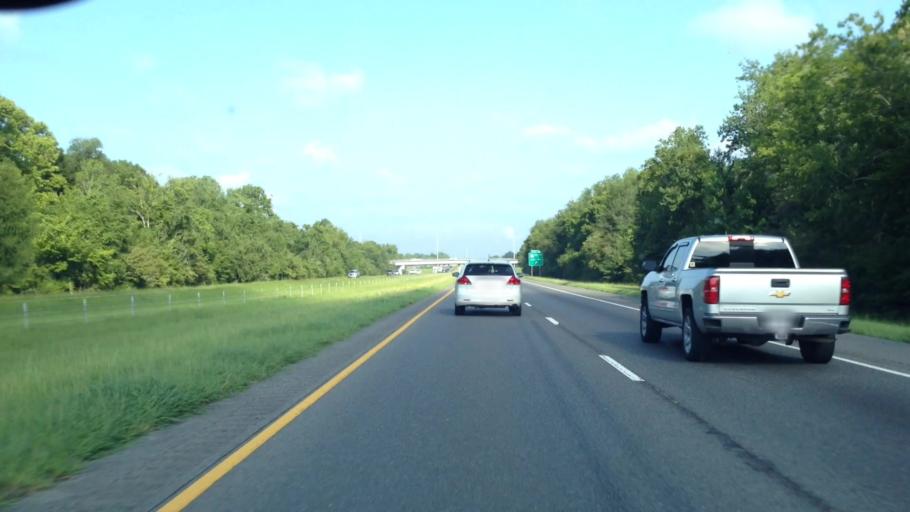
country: US
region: Louisiana
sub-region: Ascension Parish
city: Sorrento
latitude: 30.1520
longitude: -90.7955
